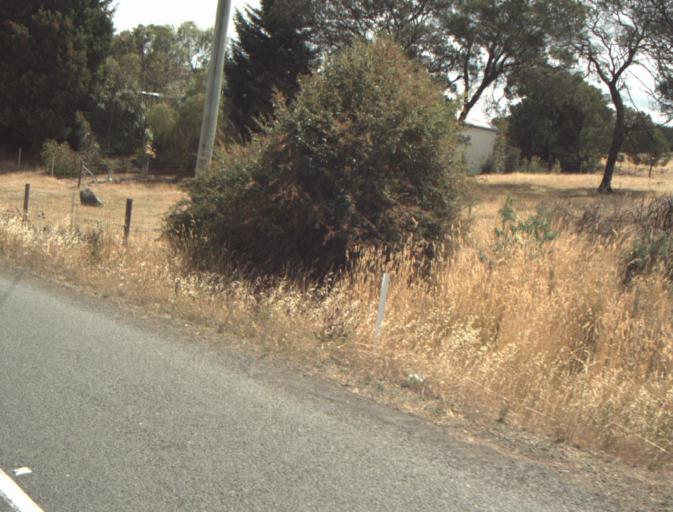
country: AU
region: Tasmania
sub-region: Northern Midlands
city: Evandale
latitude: -41.5097
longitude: 147.2874
